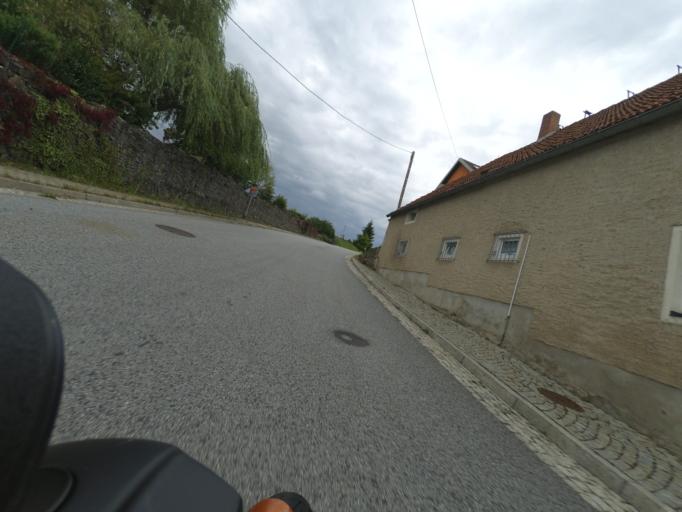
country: DE
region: Saxony
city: Reinhardtsgrimma
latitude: 50.9073
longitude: 13.7461
